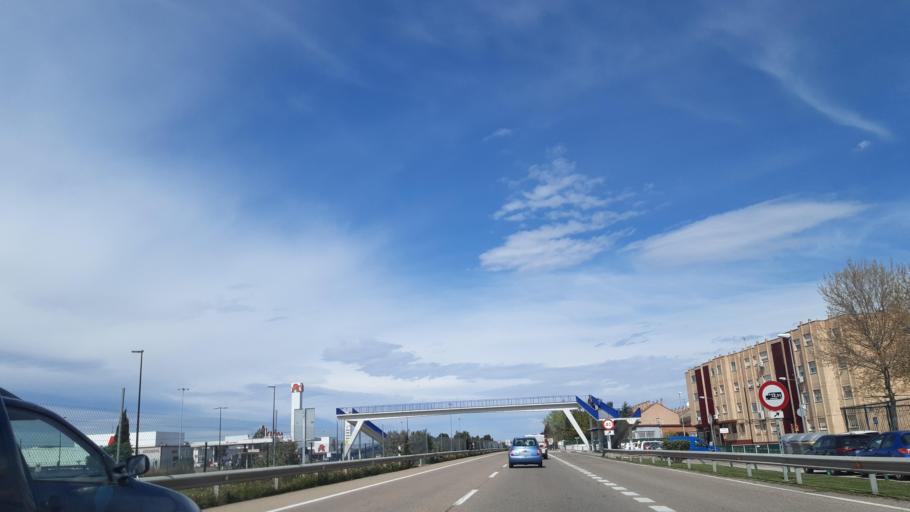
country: ES
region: Aragon
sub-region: Provincia de Zaragoza
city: Utebo
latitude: 41.7014
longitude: -0.9991
